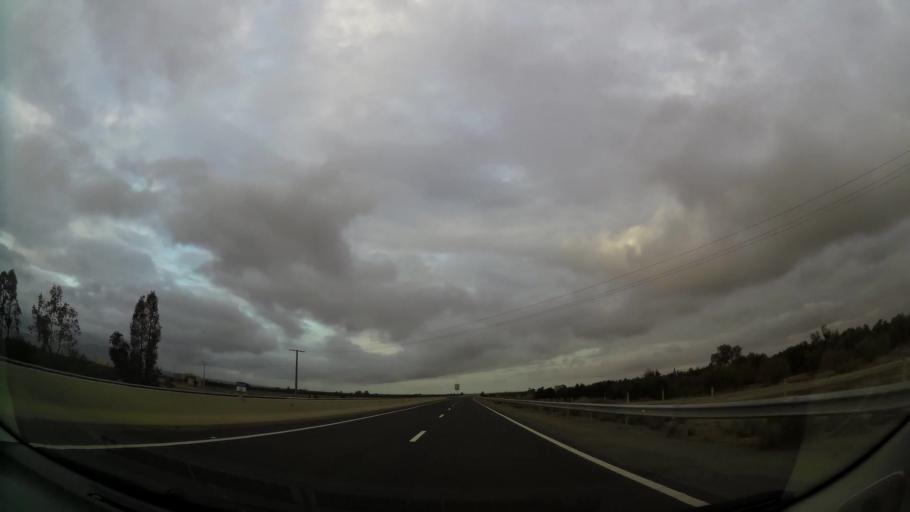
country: MA
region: Taza-Al Hoceima-Taounate
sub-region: Taza
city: Guercif
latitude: 34.3555
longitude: -3.3048
